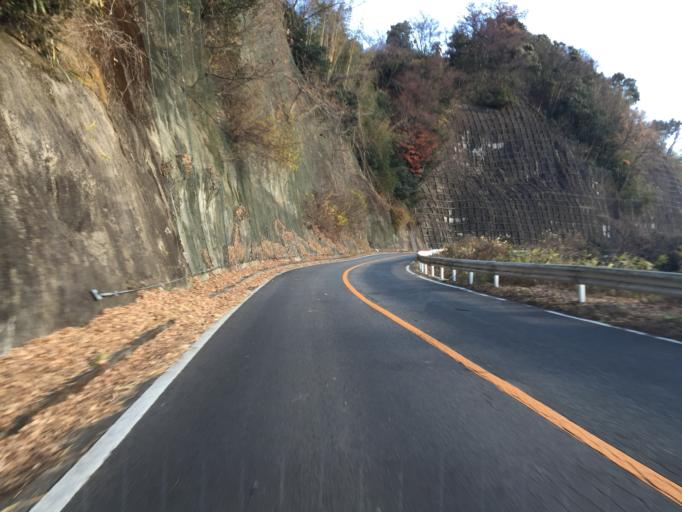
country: JP
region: Fukushima
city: Iwaki
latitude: 37.1444
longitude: 140.8375
